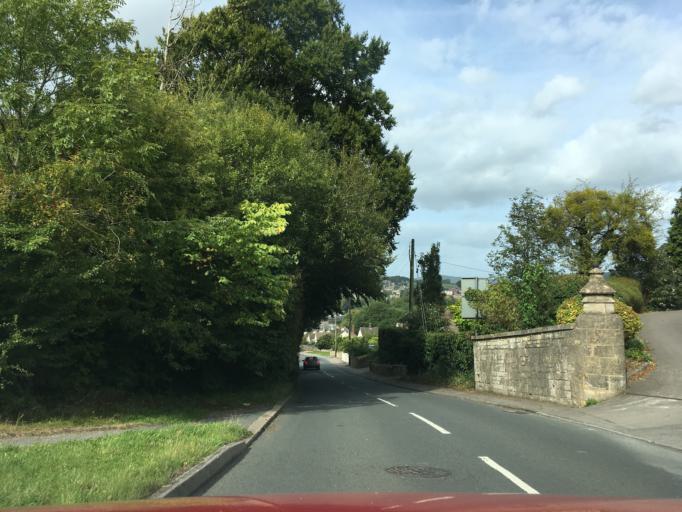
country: GB
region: England
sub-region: Gloucestershire
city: Stroud
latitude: 51.7355
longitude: -2.2411
